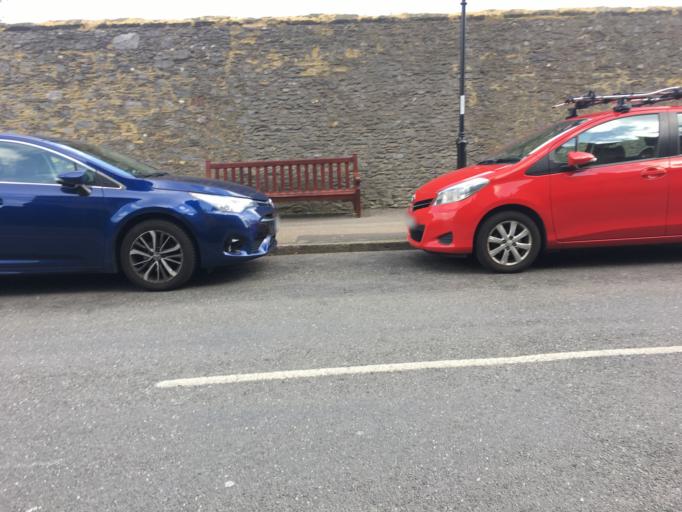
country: GB
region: England
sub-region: West Sussex
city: Arundel
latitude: 50.8554
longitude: -0.5592
